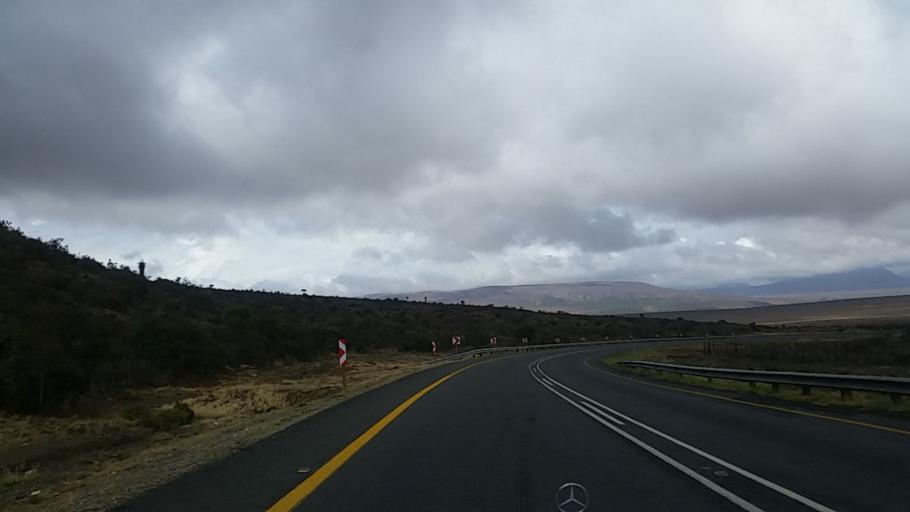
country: ZA
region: Eastern Cape
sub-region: Cacadu District Municipality
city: Graaff-Reinet
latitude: -32.1159
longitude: 24.6085
